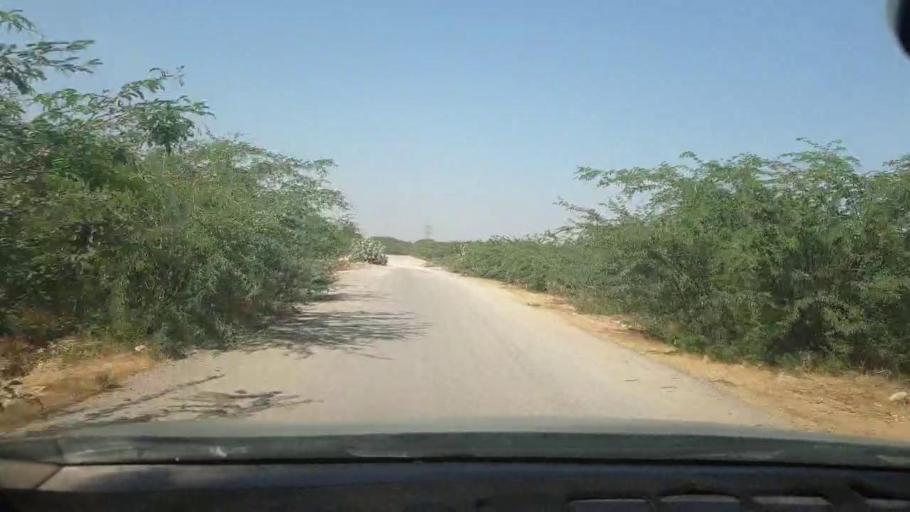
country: PK
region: Sindh
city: Malir Cantonment
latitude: 25.1609
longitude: 67.1619
